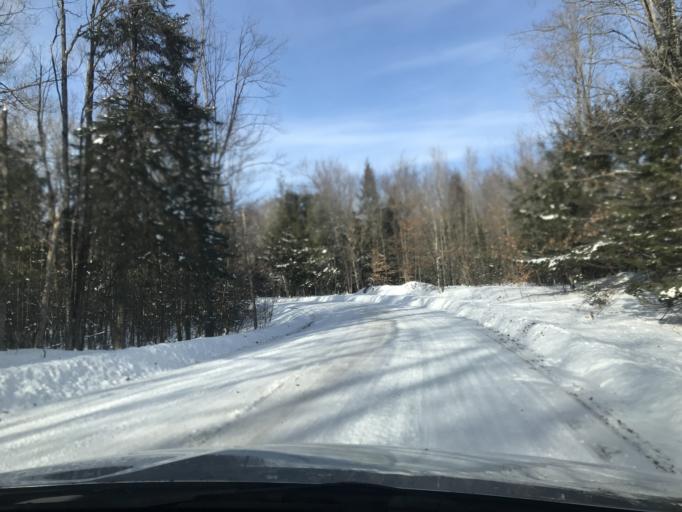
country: US
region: Wisconsin
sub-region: Oconto County
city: Gillett
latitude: 45.1471
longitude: -88.2351
